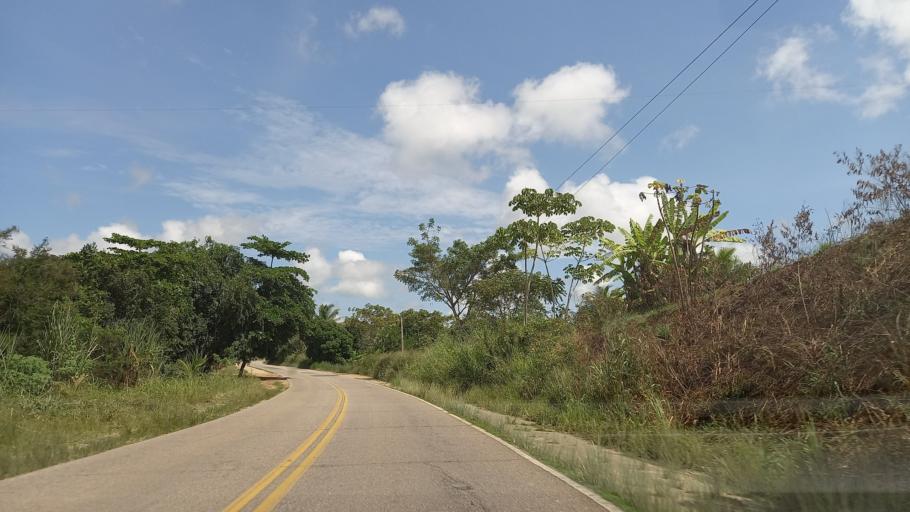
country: BR
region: Pernambuco
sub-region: Barreiros
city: Barreiros
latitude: -8.7732
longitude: -35.1732
